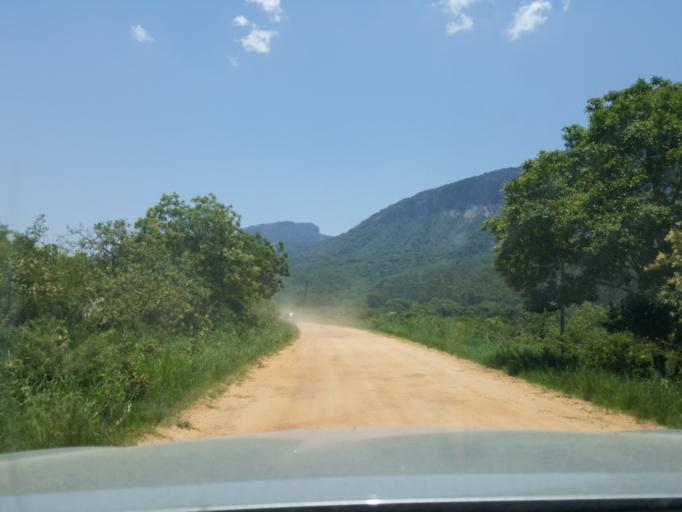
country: ZA
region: Limpopo
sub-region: Mopani District Municipality
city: Hoedspruit
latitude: -24.5964
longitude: 30.9178
